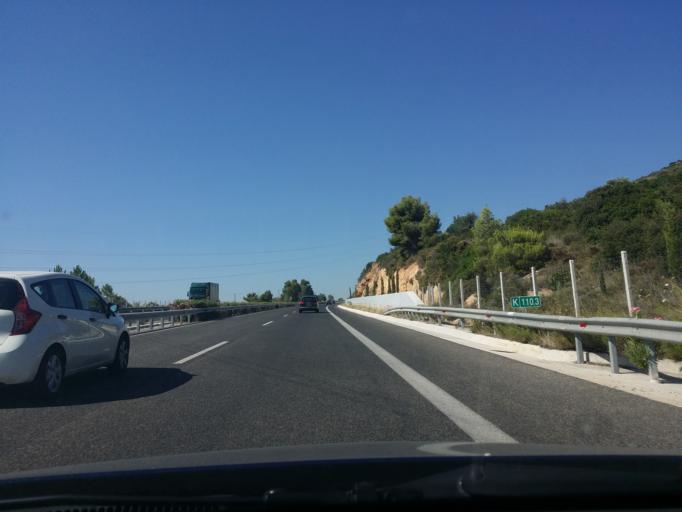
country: GR
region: Peloponnese
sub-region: Nomos Korinthias
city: Nemea
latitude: 37.7909
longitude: 22.7133
